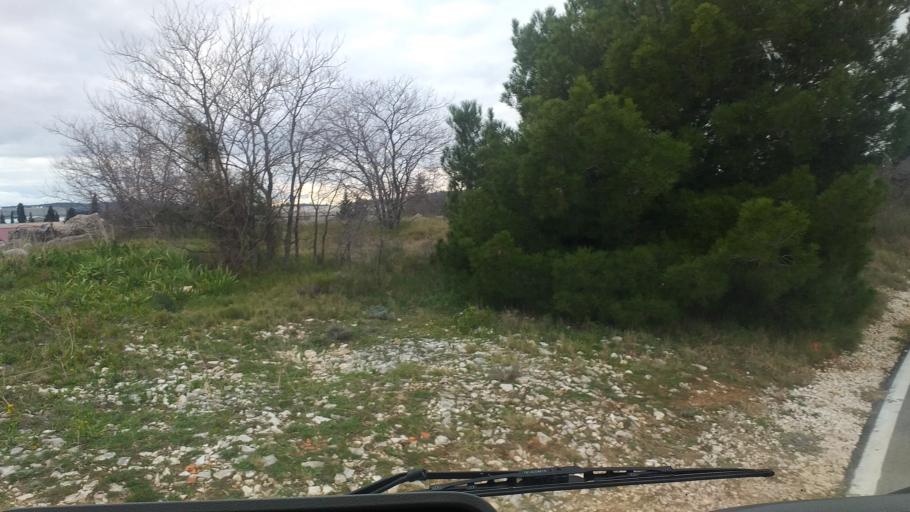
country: HR
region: Sibensko-Kniniska
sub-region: Grad Sibenik
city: Sibenik
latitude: 43.7156
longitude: 15.9100
